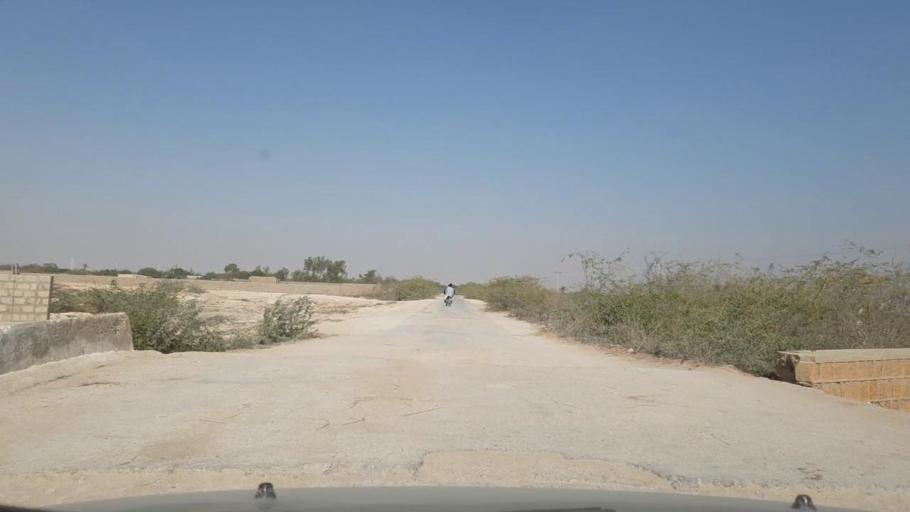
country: PK
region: Sindh
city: Daro Mehar
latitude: 25.0104
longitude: 68.0148
